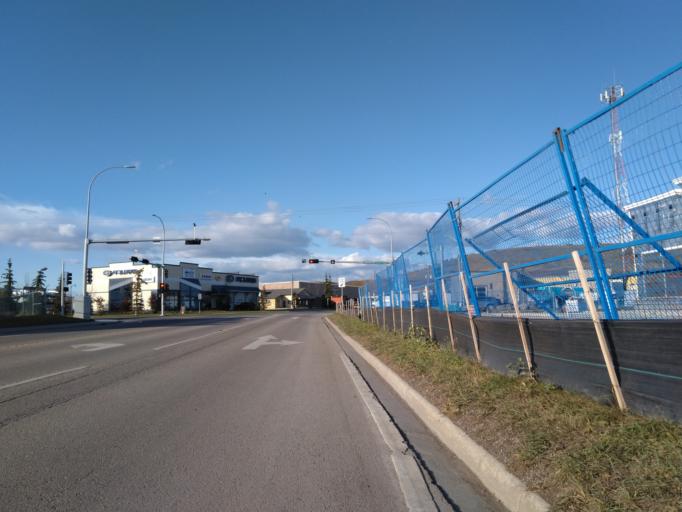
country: CA
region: Alberta
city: Cochrane
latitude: 51.1827
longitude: -114.4667
